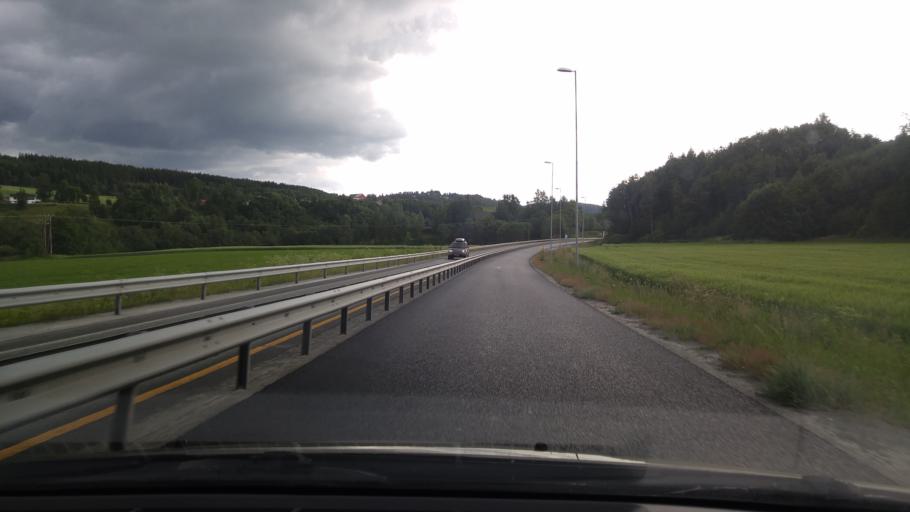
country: NO
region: Nord-Trondelag
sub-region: Levanger
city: Levanger
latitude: 63.7352
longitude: 11.3213
